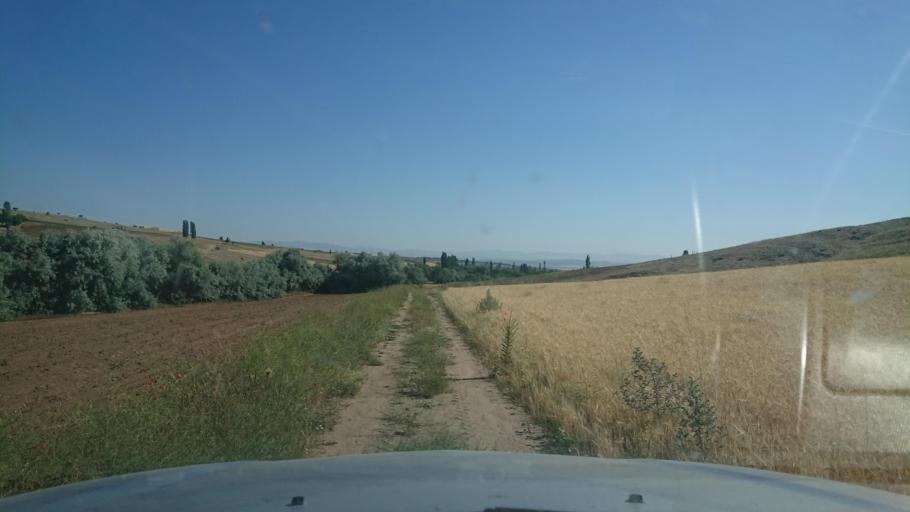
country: TR
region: Aksaray
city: Agacoren
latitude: 38.8433
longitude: 33.9263
